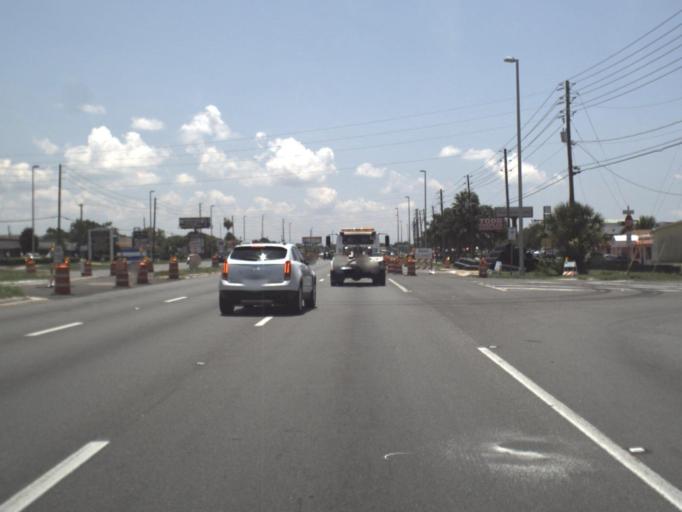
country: US
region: Florida
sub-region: Pasco County
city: Bayonet Point
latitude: 28.3161
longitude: -82.6994
